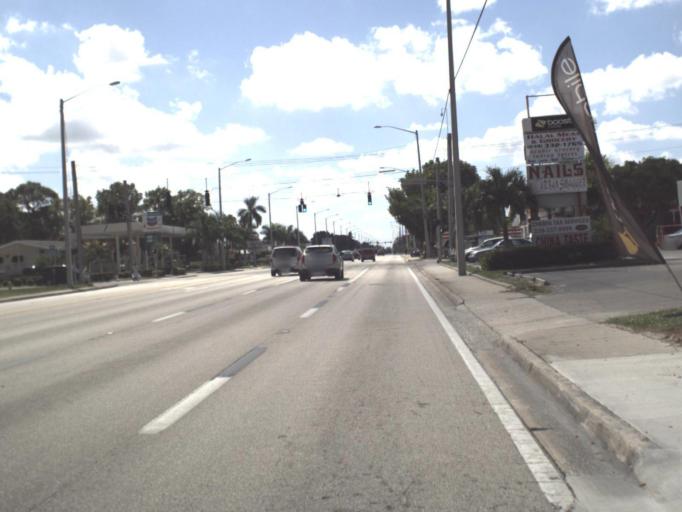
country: US
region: Florida
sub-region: Lee County
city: Fort Myers
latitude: 26.6234
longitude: -81.8723
